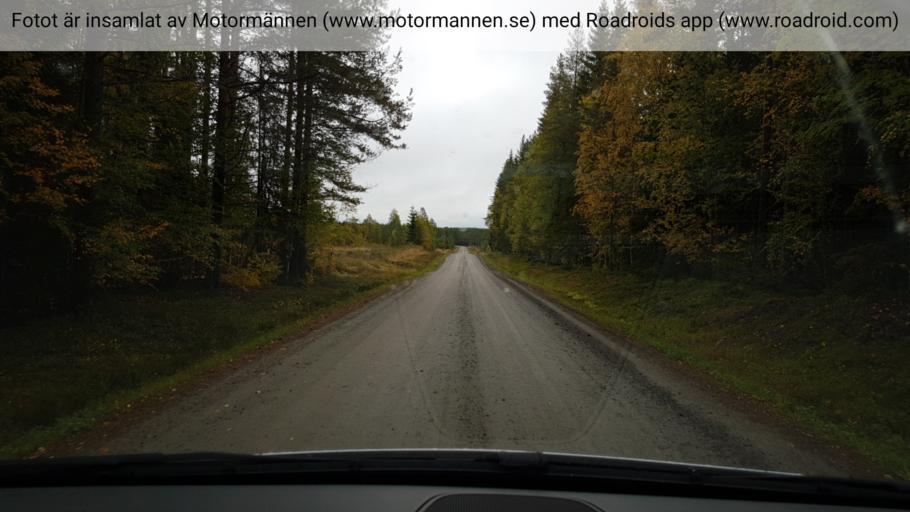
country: SE
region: Vaesterbotten
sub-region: Umea Kommun
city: Ersmark
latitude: 64.1036
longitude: 20.3022
